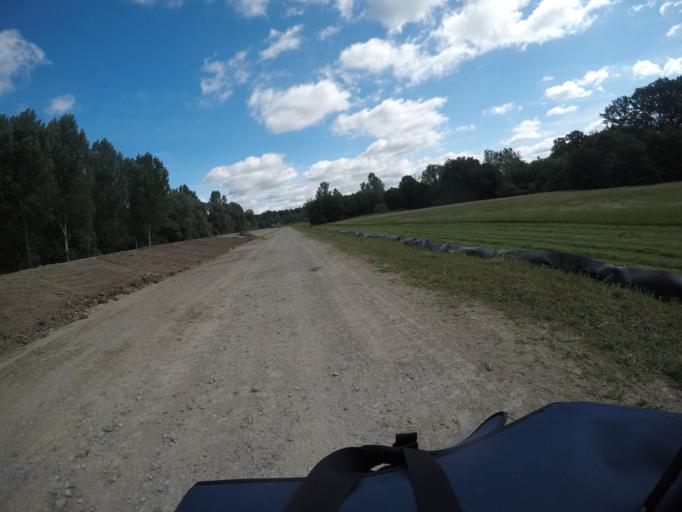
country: DE
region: Baden-Wuerttemberg
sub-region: Karlsruhe Region
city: Au am Rhein
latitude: 48.9527
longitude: 8.2140
